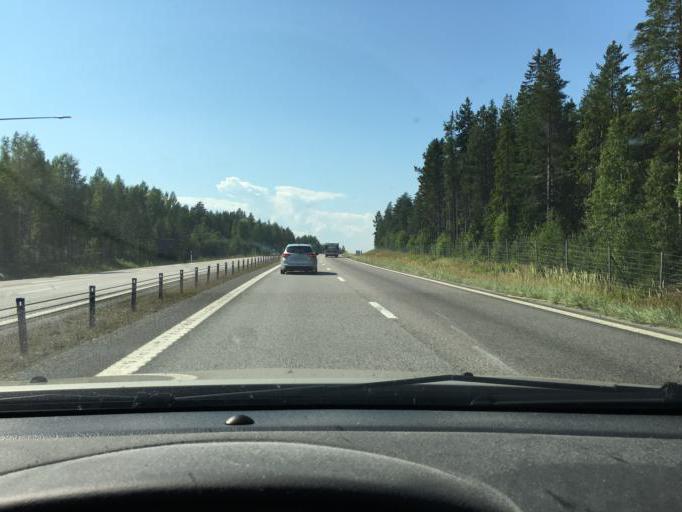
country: SE
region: Norrbotten
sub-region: Lulea Kommun
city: Gammelstad
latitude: 65.5828
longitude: 21.9947
